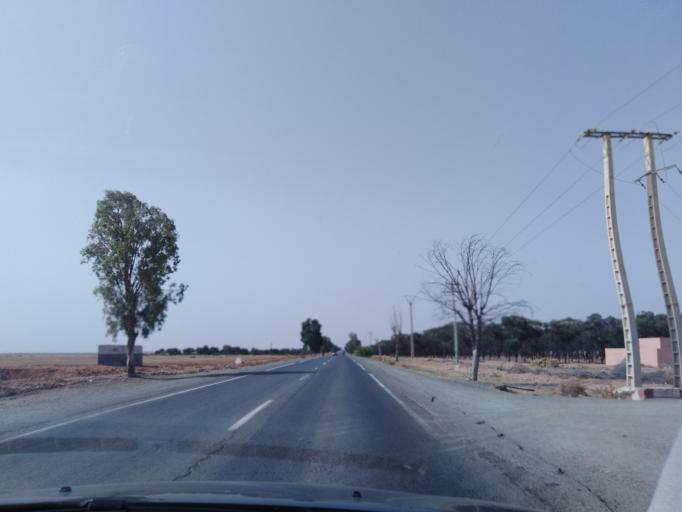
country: MA
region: Marrakech-Tensift-Al Haouz
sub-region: Kelaa-Des-Sraghna
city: Sidi Bou Othmane
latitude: 31.9890
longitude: -7.9480
